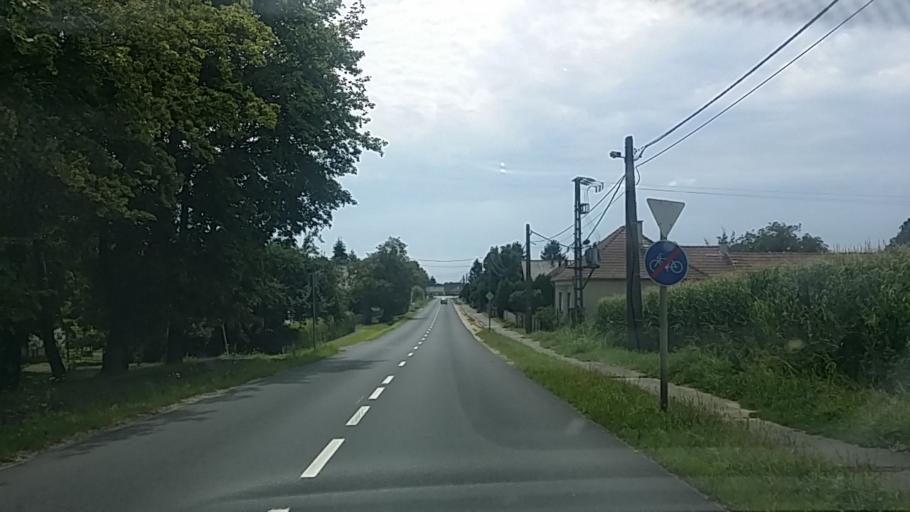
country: HR
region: Medimurska
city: Podturen
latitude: 46.5200
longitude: 16.5560
